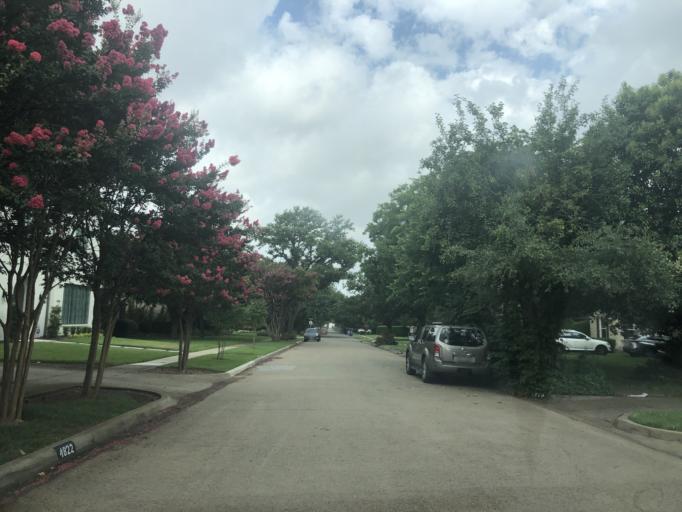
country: US
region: Texas
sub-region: Dallas County
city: University Park
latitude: 32.8532
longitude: -96.8268
